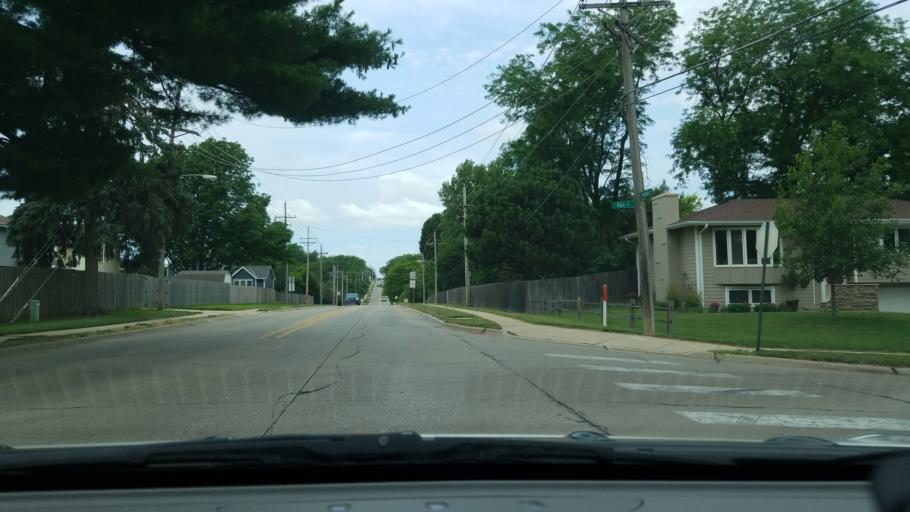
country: US
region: Nebraska
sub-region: Sarpy County
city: Papillion
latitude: 41.1436
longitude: -96.0312
